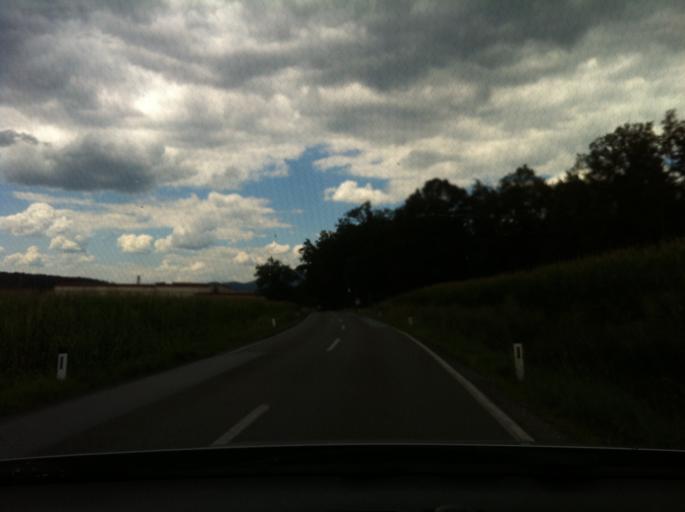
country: AT
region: Styria
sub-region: Politischer Bezirk Hartberg-Fuerstenfeld
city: Kaindorf
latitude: 47.2147
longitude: 15.9257
